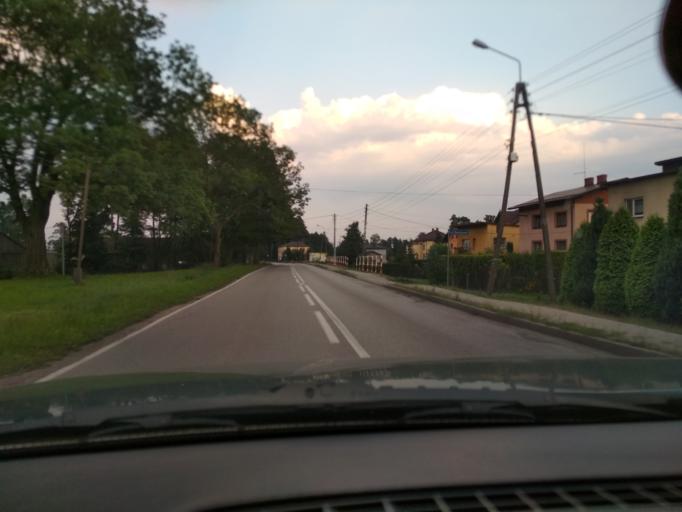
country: PL
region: Silesian Voivodeship
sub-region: Powiat cieszynski
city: Zablocie
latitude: 49.9000
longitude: 18.7888
